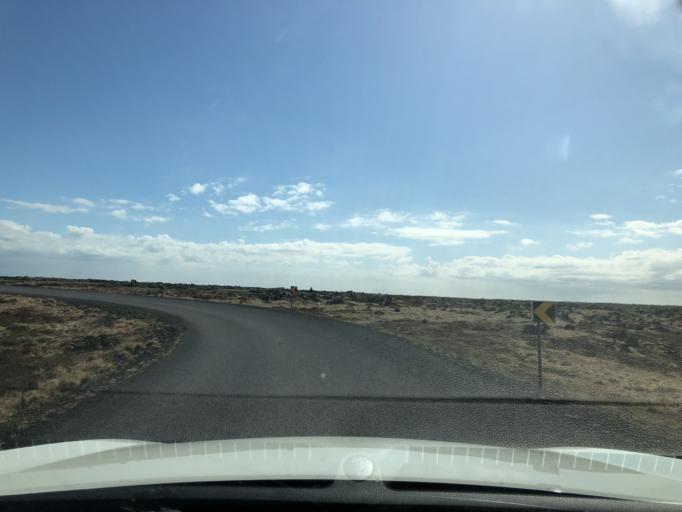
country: IS
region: West
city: Olafsvik
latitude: 64.8257
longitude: -23.3942
